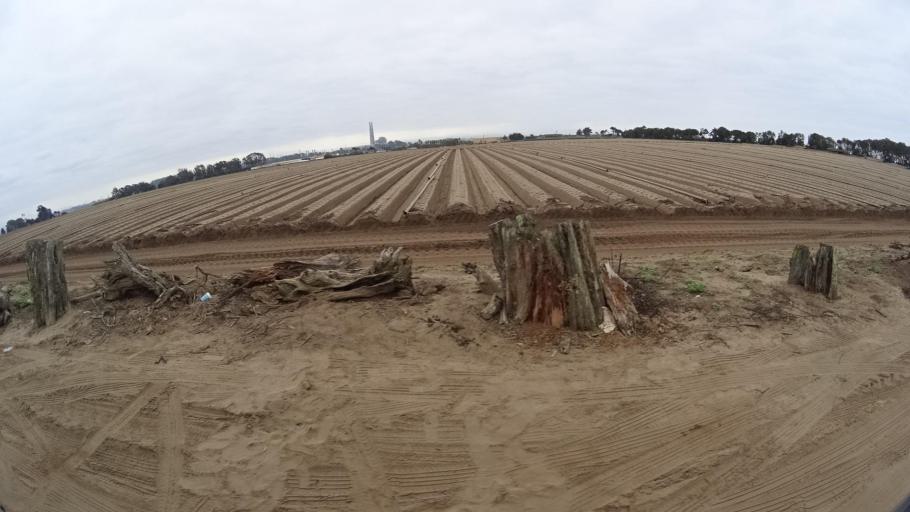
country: US
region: California
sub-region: Monterey County
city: Elkhorn
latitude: 36.8271
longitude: -121.7874
